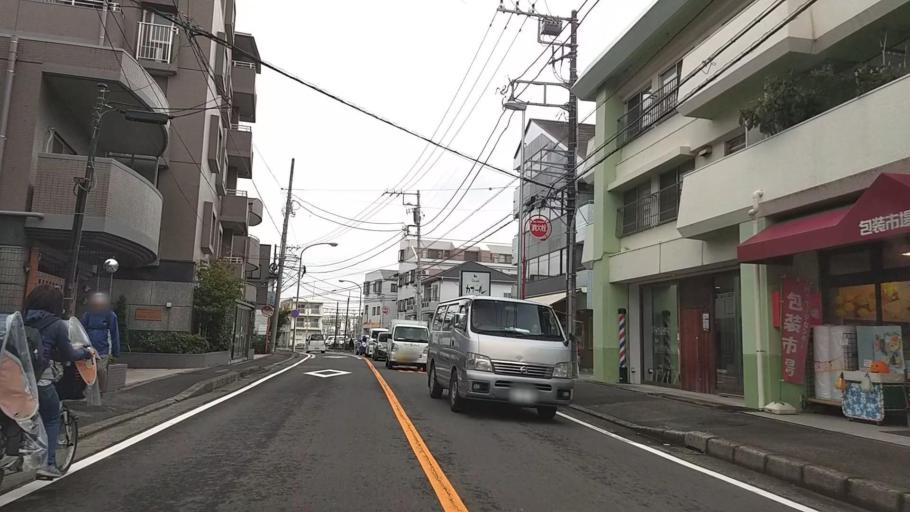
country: JP
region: Kanagawa
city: Fujisawa
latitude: 35.3970
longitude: 139.5361
